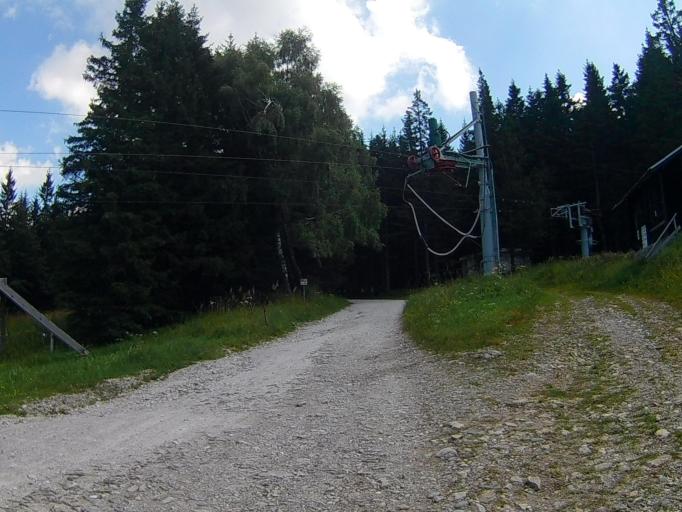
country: SI
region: Ruse
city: Ruse
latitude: 46.4989
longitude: 15.4955
